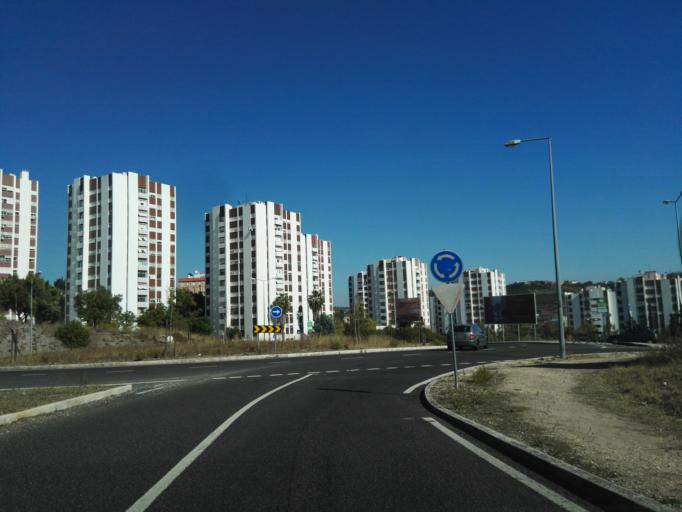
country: PT
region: Lisbon
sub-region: Odivelas
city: Povoa de Santo Adriao
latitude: 38.8078
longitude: -9.1634
